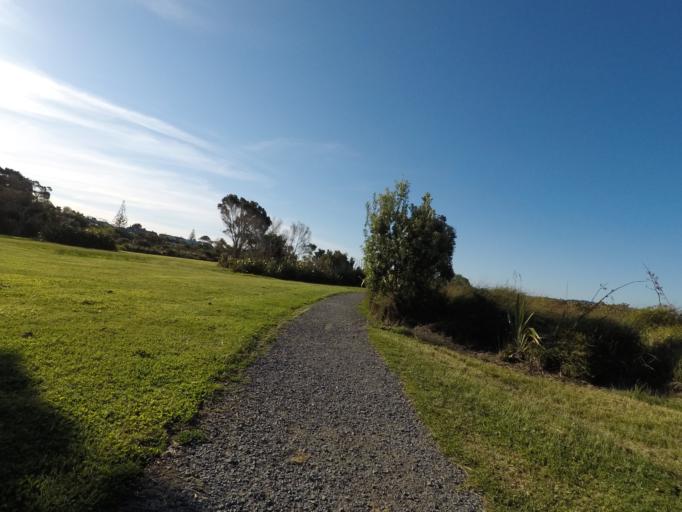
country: NZ
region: Auckland
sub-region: Auckland
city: Rosebank
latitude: -36.8276
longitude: 174.6541
